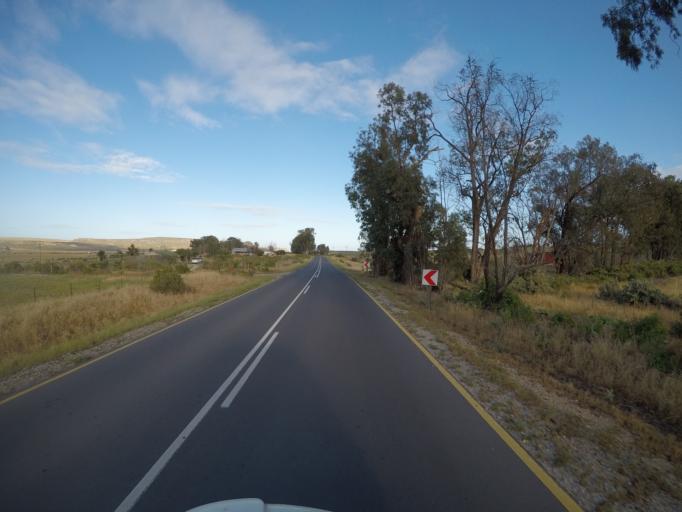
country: ZA
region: Western Cape
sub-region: West Coast District Municipality
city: Clanwilliam
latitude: -32.3115
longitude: 18.3831
